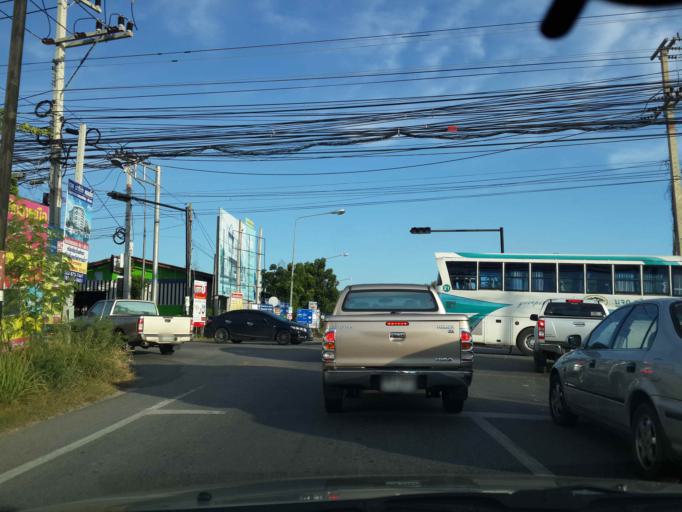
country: TH
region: Chon Buri
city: Phatthaya
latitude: 12.8826
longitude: 100.9045
